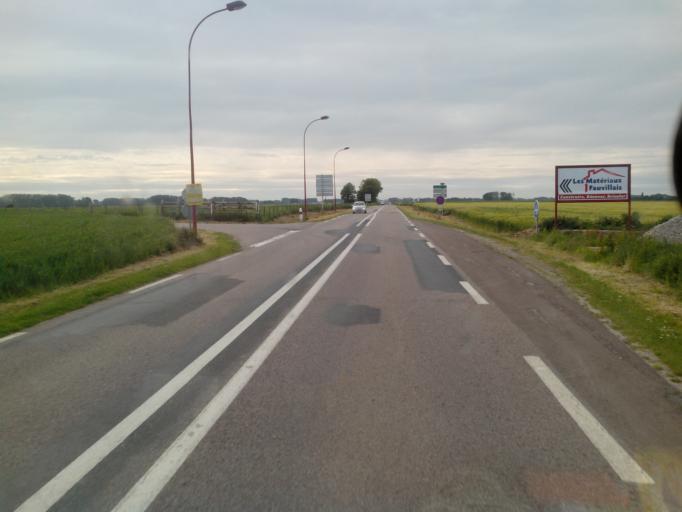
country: FR
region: Haute-Normandie
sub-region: Departement de la Seine-Maritime
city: Fauville-en-Caux
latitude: 49.6607
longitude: 0.5903
